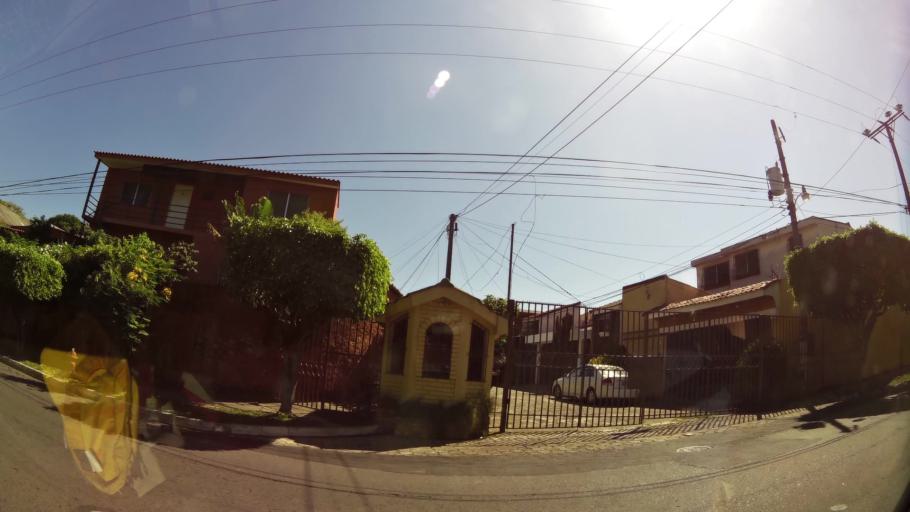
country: SV
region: La Libertad
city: Nuevo Cuscatlan
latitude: 13.6496
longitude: -89.2791
